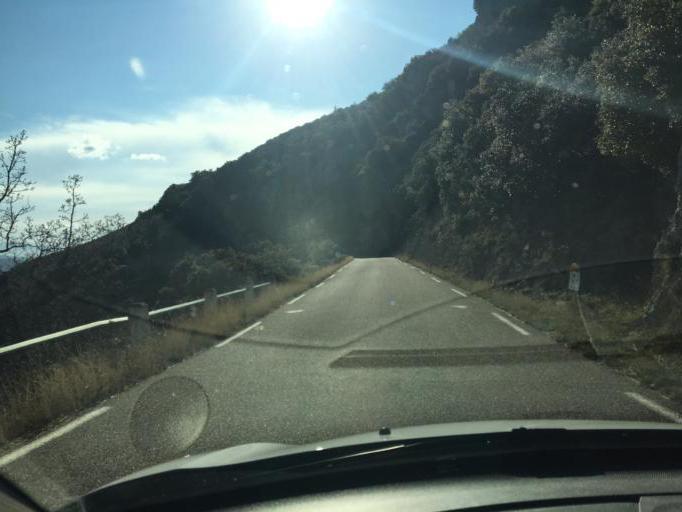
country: FR
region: Provence-Alpes-Cote d'Azur
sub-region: Departement du Vaucluse
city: Villes-sur-Auzon
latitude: 44.0569
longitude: 5.2976
